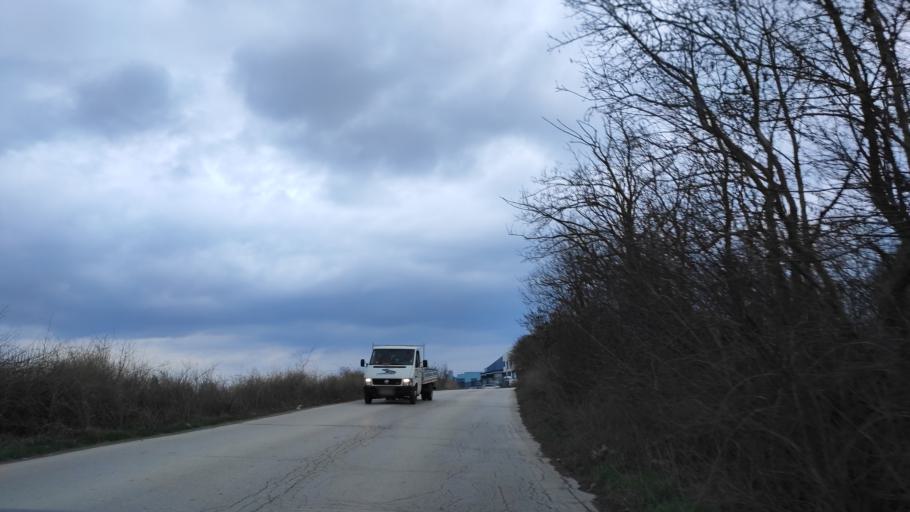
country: BG
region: Varna
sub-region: Obshtina Aksakovo
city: Aksakovo
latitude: 43.2278
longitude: 27.8053
